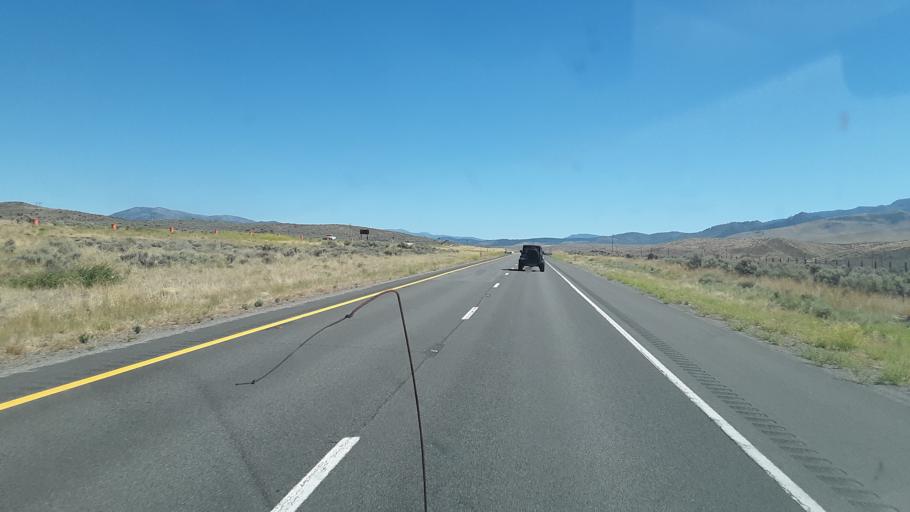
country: US
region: Nevada
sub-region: Washoe County
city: Cold Springs
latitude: 39.7269
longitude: -120.0388
